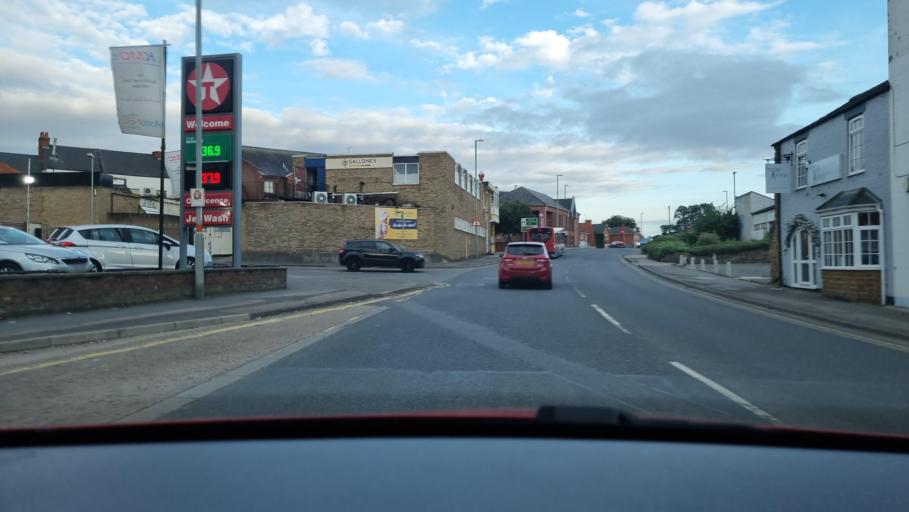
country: GB
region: England
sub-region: Northamptonshire
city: Northampton
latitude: 52.2641
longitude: -0.9014
